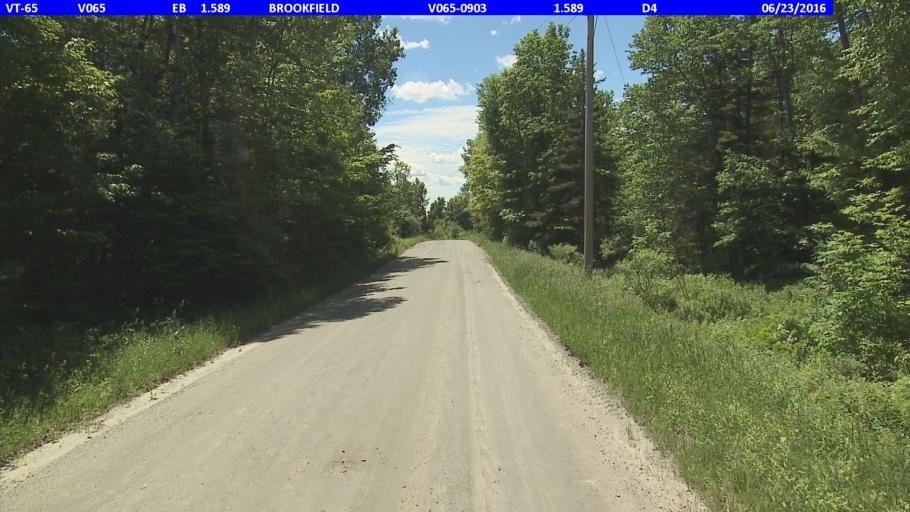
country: US
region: Vermont
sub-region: Washington County
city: Northfield
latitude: 44.0481
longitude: -72.6257
